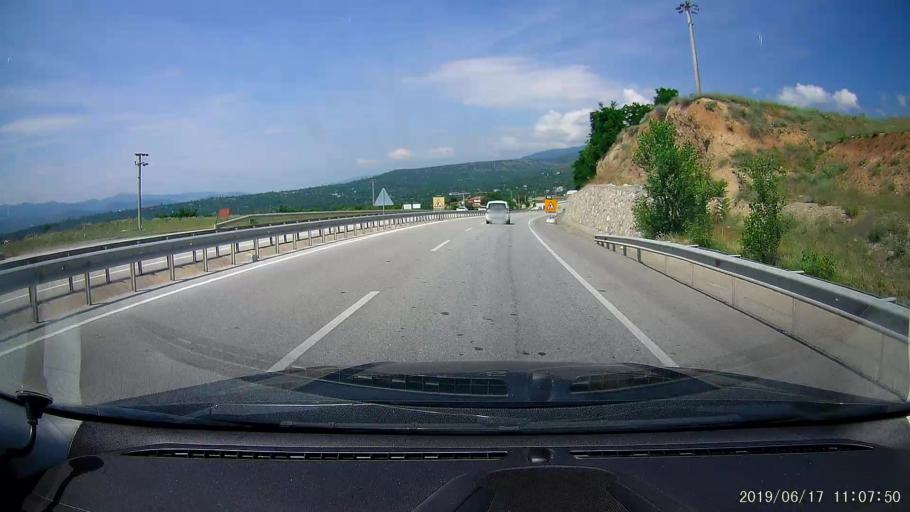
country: TR
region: Kastamonu
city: Tosya
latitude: 40.9995
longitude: 34.0484
